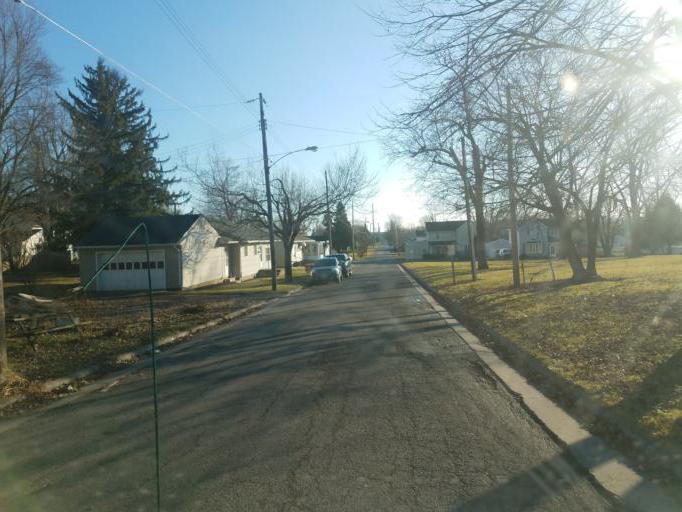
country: US
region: Ohio
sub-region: Hardin County
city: Kenton
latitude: 40.6457
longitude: -83.5981
